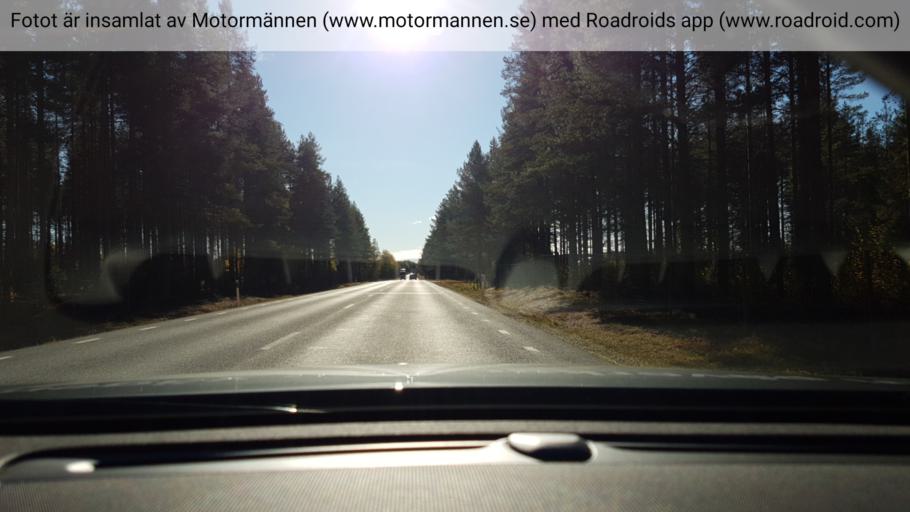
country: SE
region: Vaesterbotten
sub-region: Skelleftea Kommun
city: Burea
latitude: 64.5616
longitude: 21.2346
